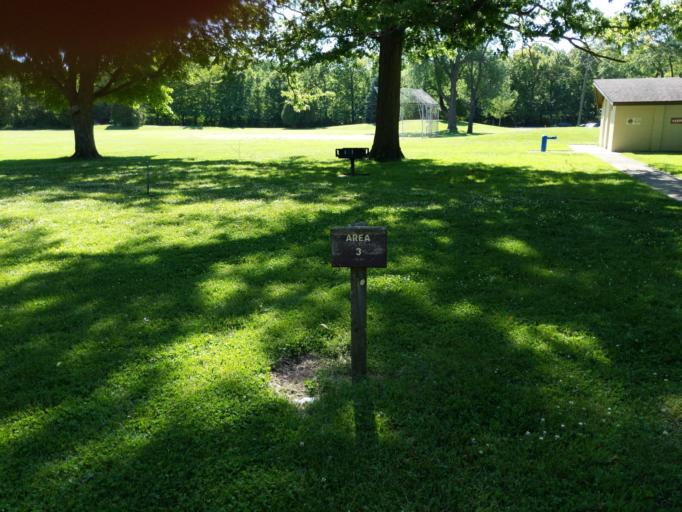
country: US
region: Michigan
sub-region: Eaton County
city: Grand Ledge
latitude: 42.7600
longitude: -84.7610
